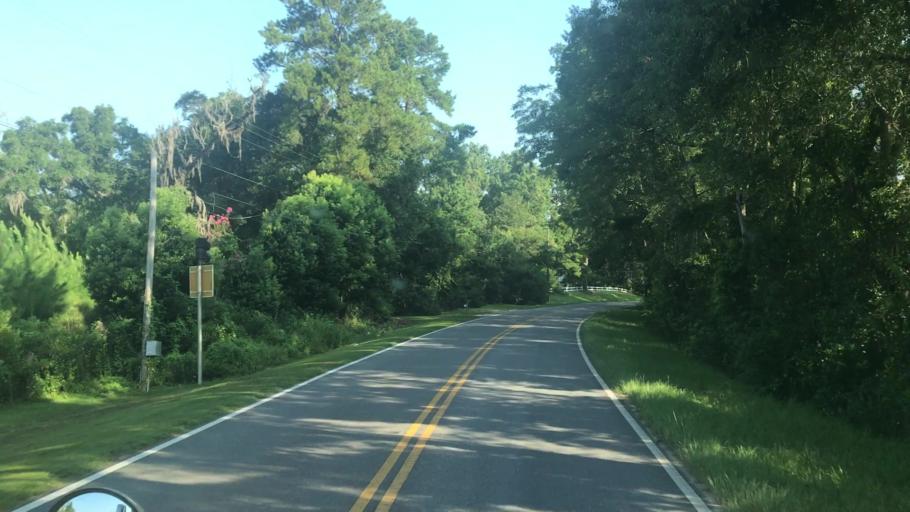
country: US
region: Florida
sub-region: Gadsden County
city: Quincy
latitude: 30.6076
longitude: -84.5734
